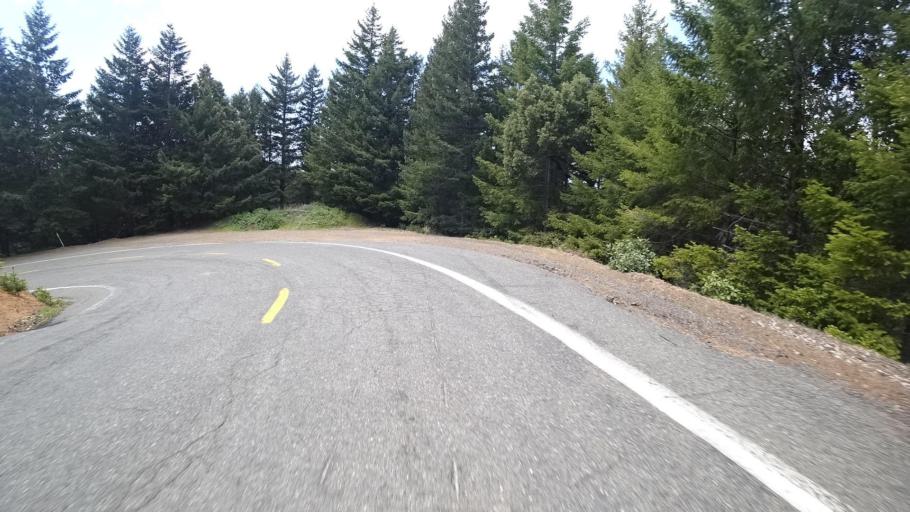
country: US
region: California
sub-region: Humboldt County
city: Redway
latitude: 40.0443
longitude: -124.0237
